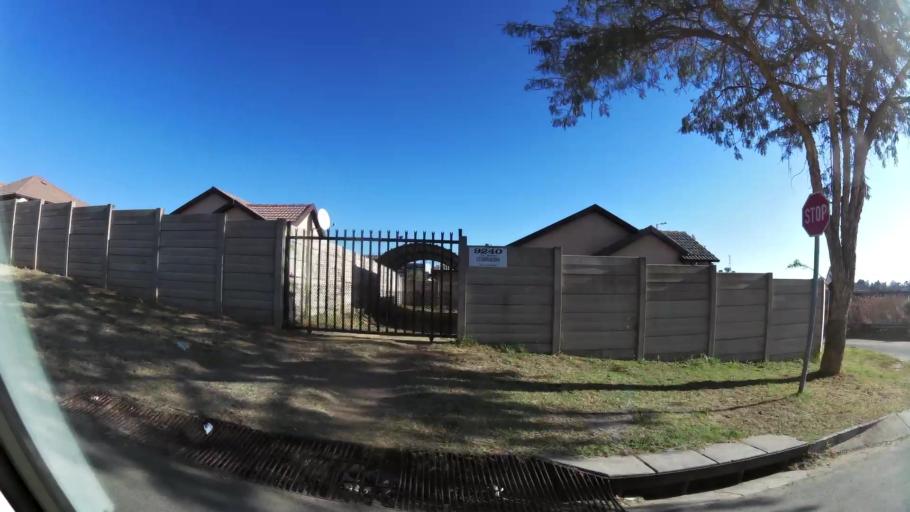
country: ZA
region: Gauteng
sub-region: City of Tshwane Metropolitan Municipality
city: Centurion
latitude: -25.8949
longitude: 28.1019
